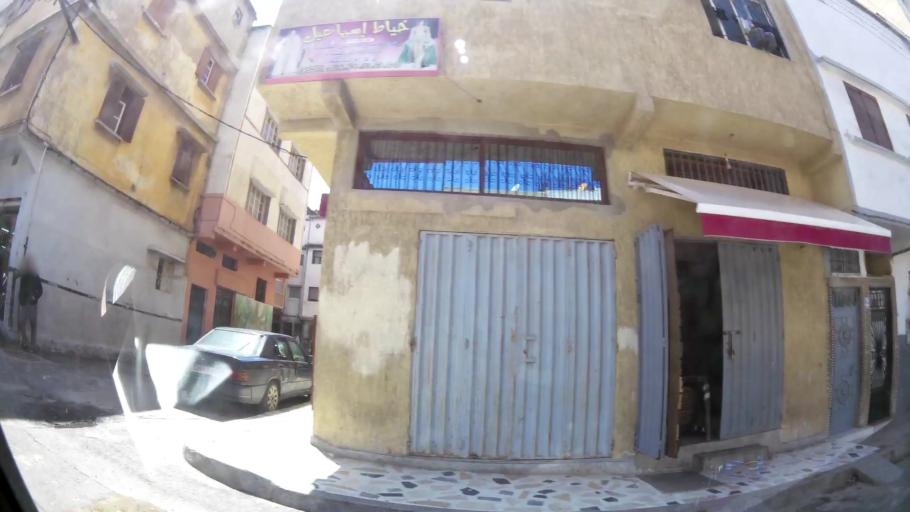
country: MA
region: Grand Casablanca
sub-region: Casablanca
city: Casablanca
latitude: 33.5628
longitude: -7.5705
